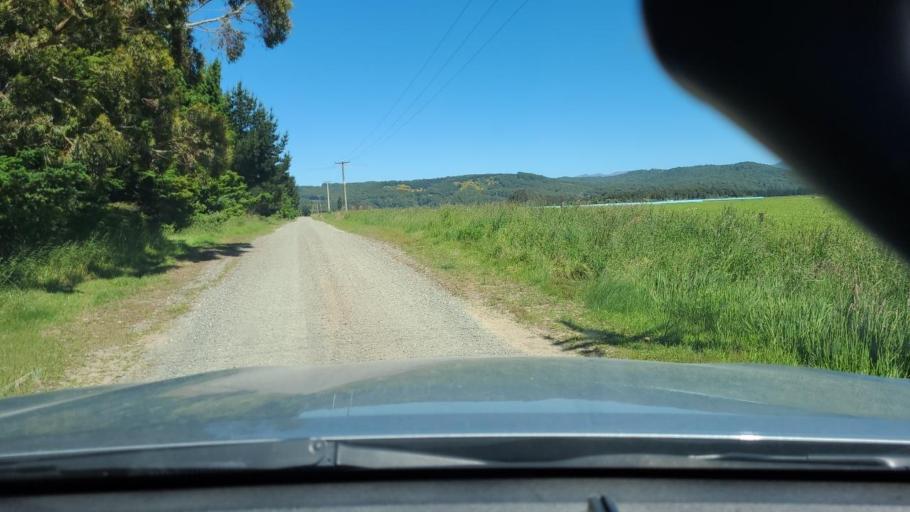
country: NZ
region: Southland
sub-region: Southland District
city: Riverton
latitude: -45.9712
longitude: 167.7056
